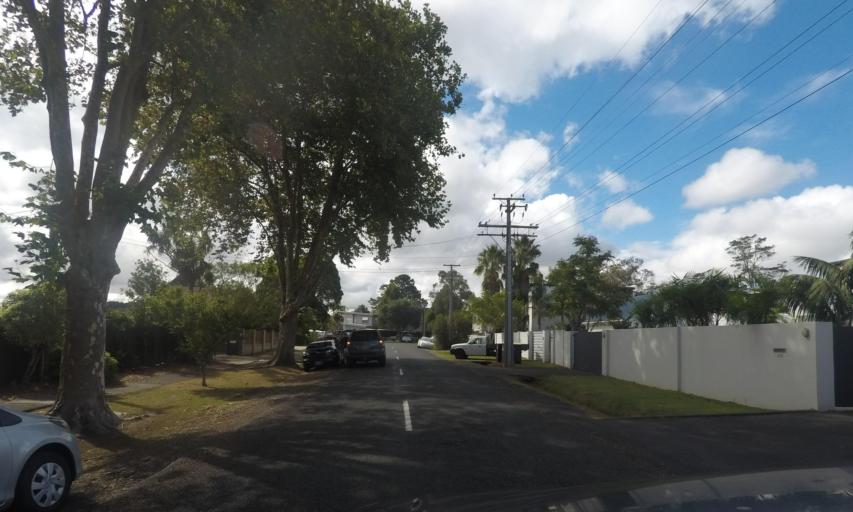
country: NZ
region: Auckland
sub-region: Auckland
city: North Shore
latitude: -36.7777
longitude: 174.6609
